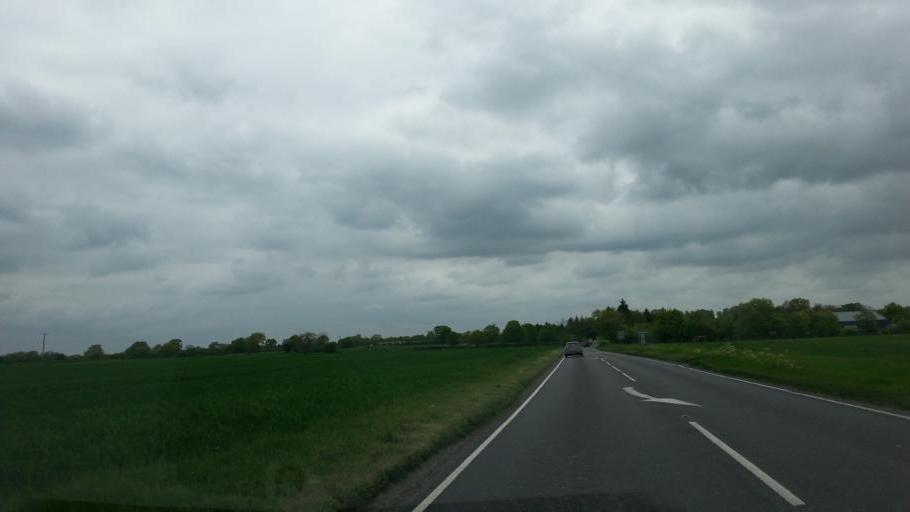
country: GB
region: England
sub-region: Suffolk
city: Lavenham
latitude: 52.1716
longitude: 0.7645
